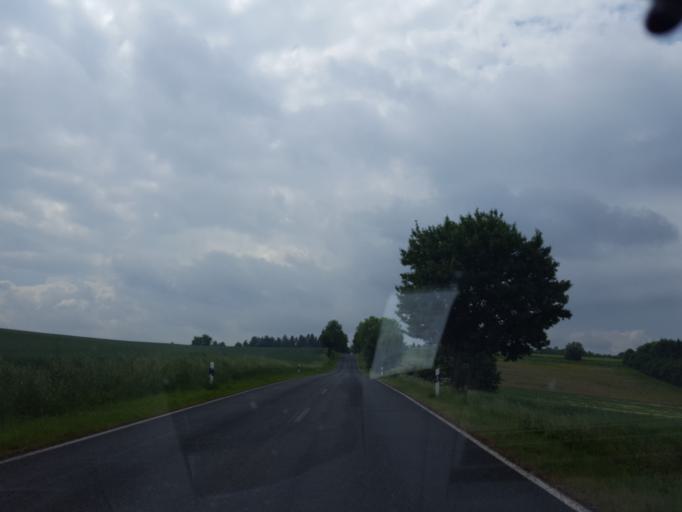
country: DE
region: Lower Saxony
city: Wulften
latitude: 51.6836
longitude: 10.1560
